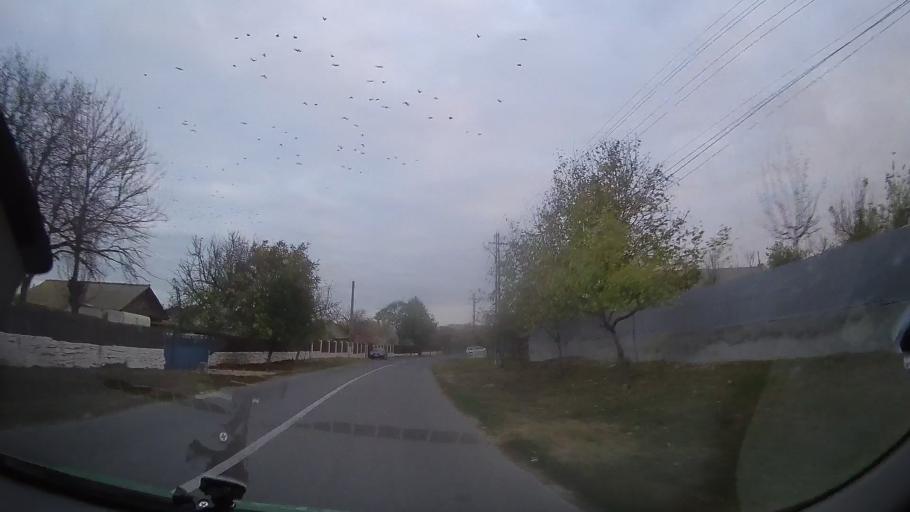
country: RO
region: Tulcea
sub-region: Comuna Mihai Bravu
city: Turda
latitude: 44.9720
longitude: 28.6270
